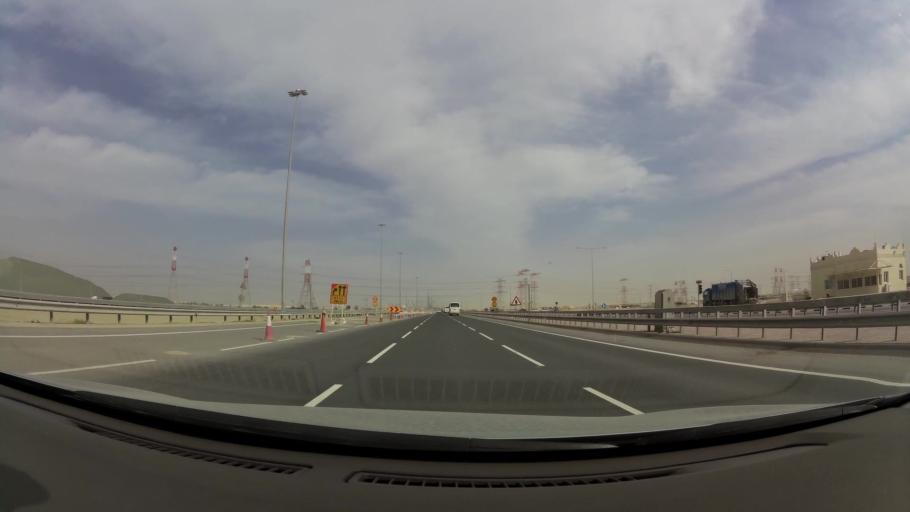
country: QA
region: Baladiyat ar Rayyan
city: Ash Shahaniyah
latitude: 25.3449
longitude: 51.3093
